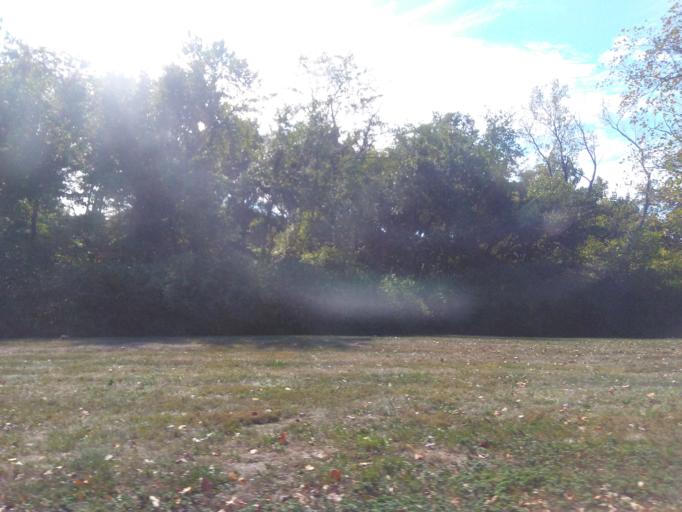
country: US
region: Missouri
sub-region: Saint Louis County
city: Concord
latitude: 38.4988
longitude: -90.3722
